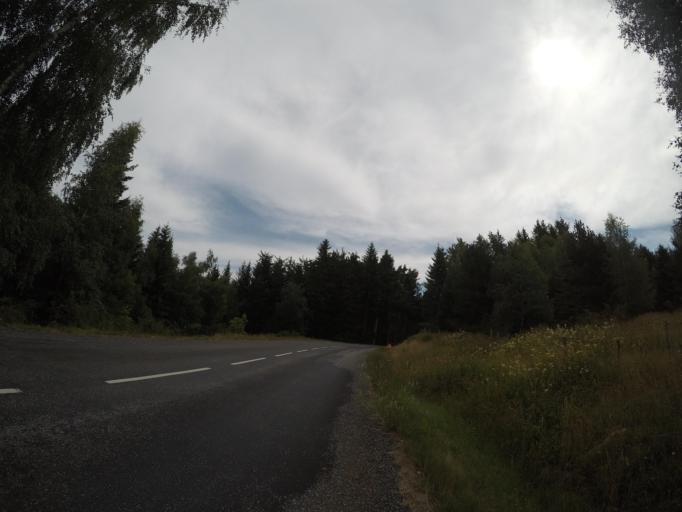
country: ES
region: Catalonia
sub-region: Provincia de Girona
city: Llivia
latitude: 42.4810
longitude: 2.0605
